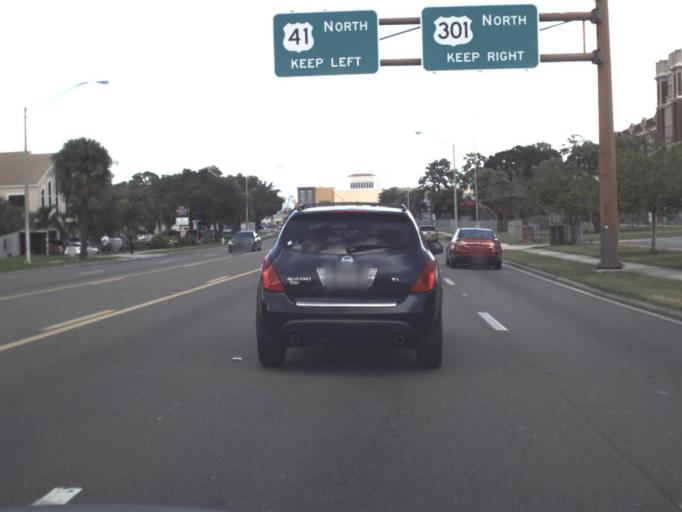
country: US
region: Florida
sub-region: Sarasota County
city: Sarasota
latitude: 27.3245
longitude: -82.5297
